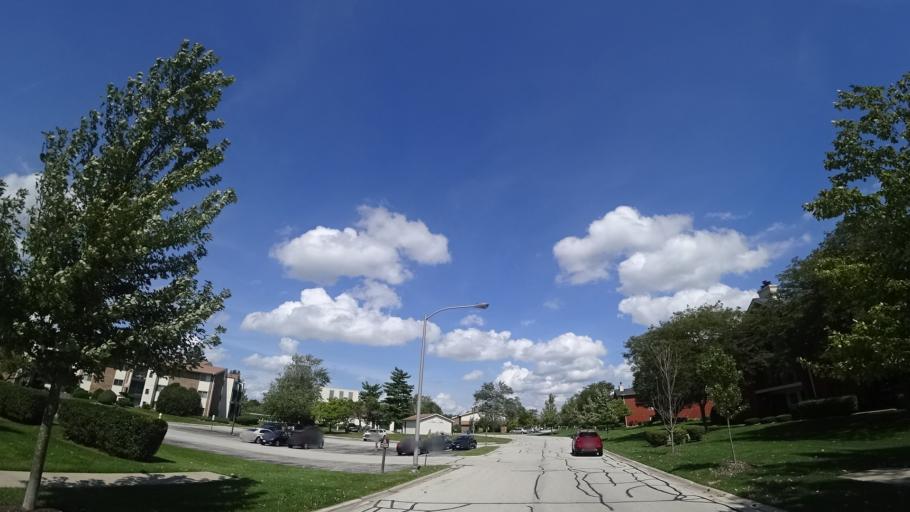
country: US
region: Illinois
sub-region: Cook County
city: Tinley Park
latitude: 41.5601
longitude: -87.7787
